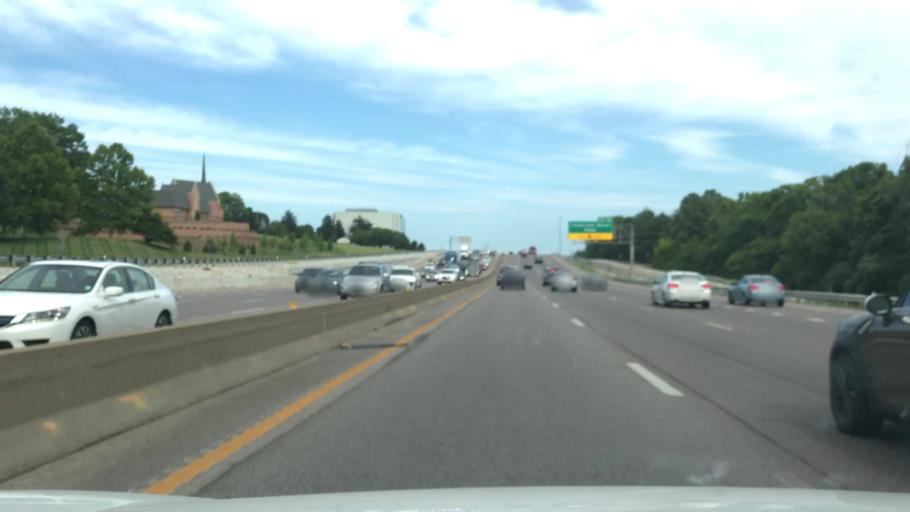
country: US
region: Missouri
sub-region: Saint Louis County
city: Chesterfield
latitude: 38.6487
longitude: -90.5408
